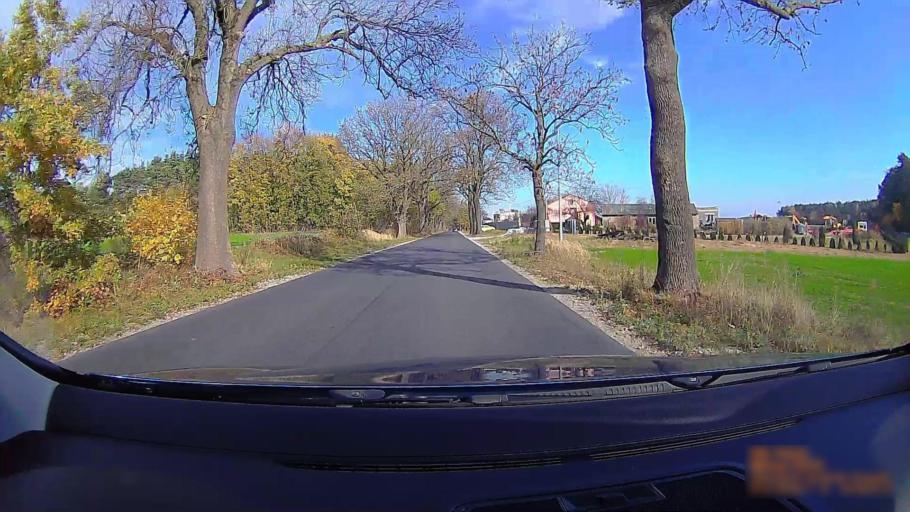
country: PL
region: Greater Poland Voivodeship
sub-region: Powiat ostrzeszowski
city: Doruchow
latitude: 51.3944
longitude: 18.0578
